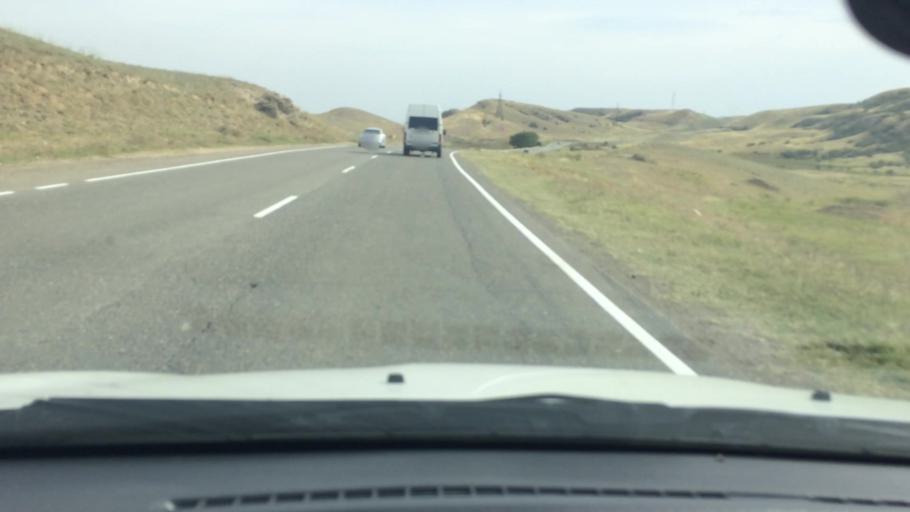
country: GE
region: Kvemo Kartli
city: Rust'avi
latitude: 41.5322
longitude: 44.9834
